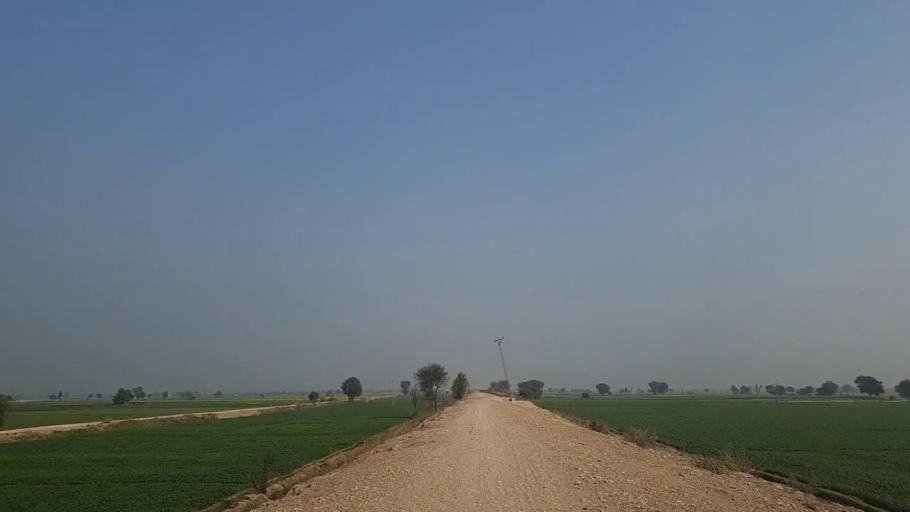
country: PK
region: Sindh
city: Sann
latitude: 26.0858
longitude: 68.1624
